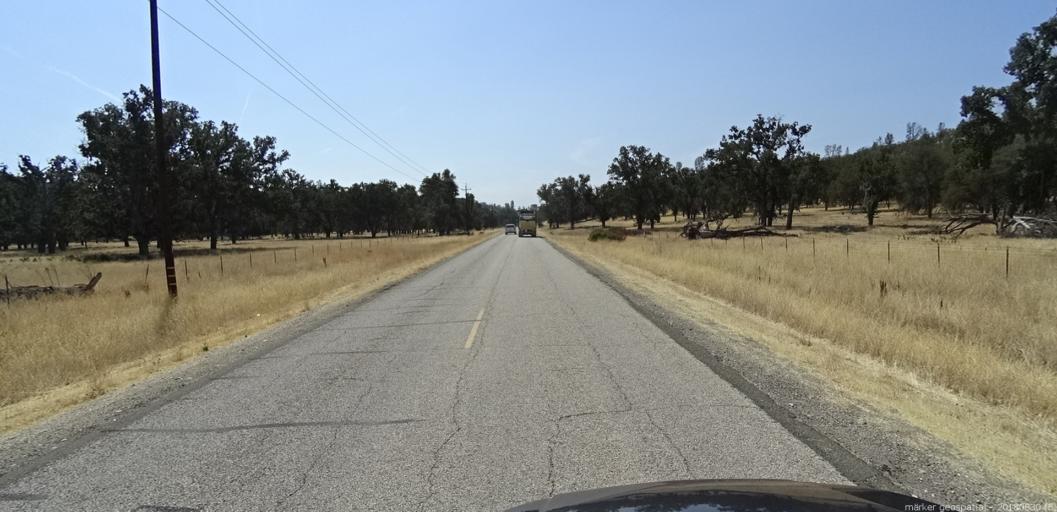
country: US
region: California
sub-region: Monterey County
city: King City
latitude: 36.0045
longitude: -121.1798
